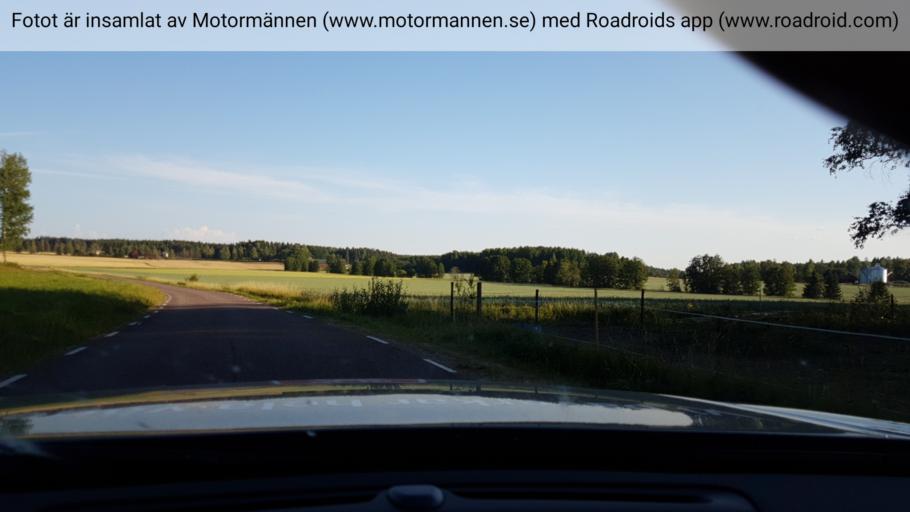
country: SE
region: Vaestmanland
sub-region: Kopings Kommun
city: Koping
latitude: 59.6412
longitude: 16.0620
